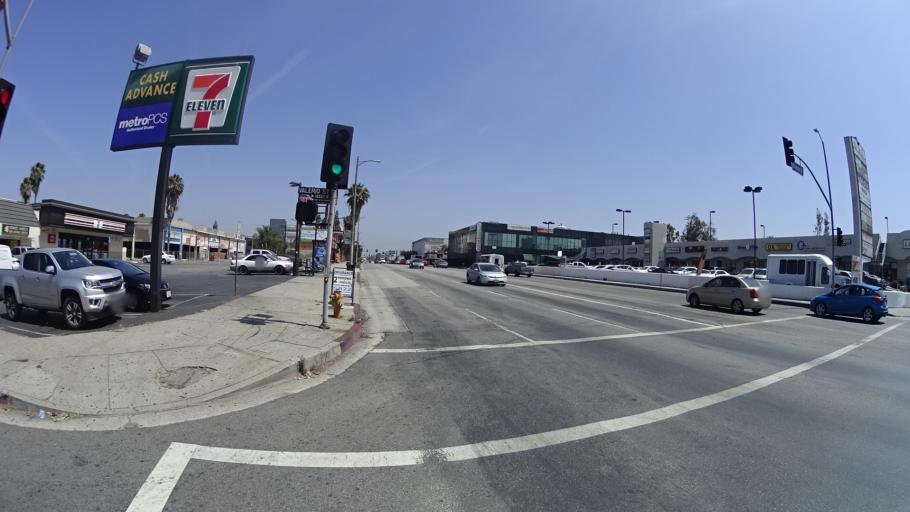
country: US
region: California
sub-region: Los Angeles County
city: Van Nuys
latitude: 34.2048
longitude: -118.4490
